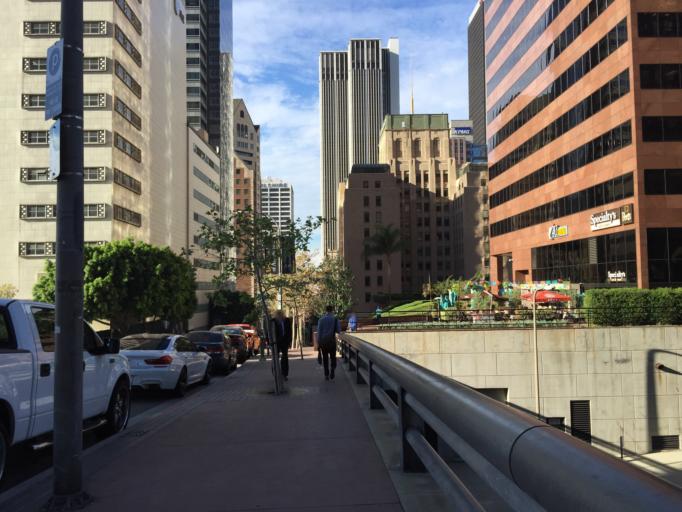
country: US
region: California
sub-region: Los Angeles County
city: Los Angeles
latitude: 34.0519
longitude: -118.2523
